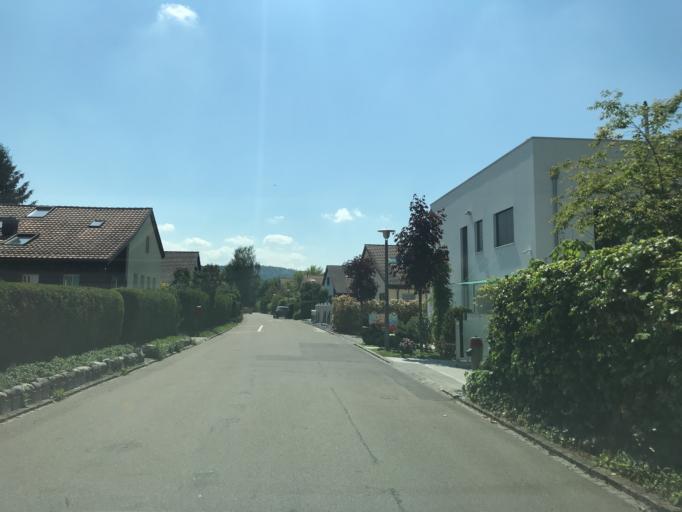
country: CH
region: Zurich
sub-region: Bezirk Winterthur
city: Toess (Kreis 4) / Vorder-Daettnau
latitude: 47.4794
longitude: 8.6989
